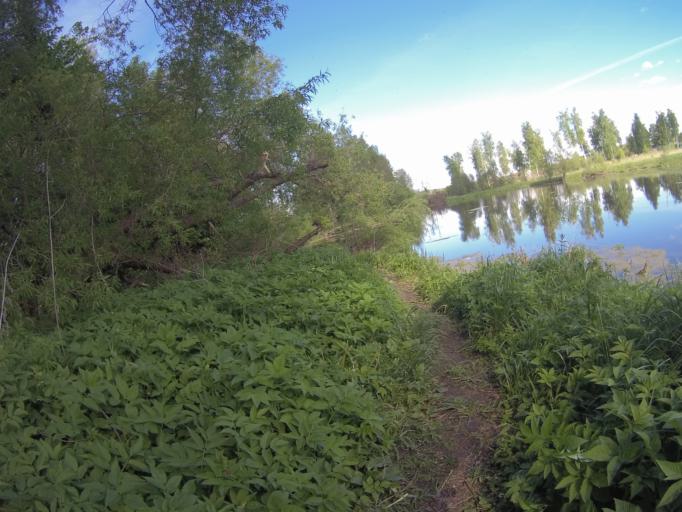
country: RU
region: Vladimir
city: Muromtsevo
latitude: 55.9271
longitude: 40.9065
